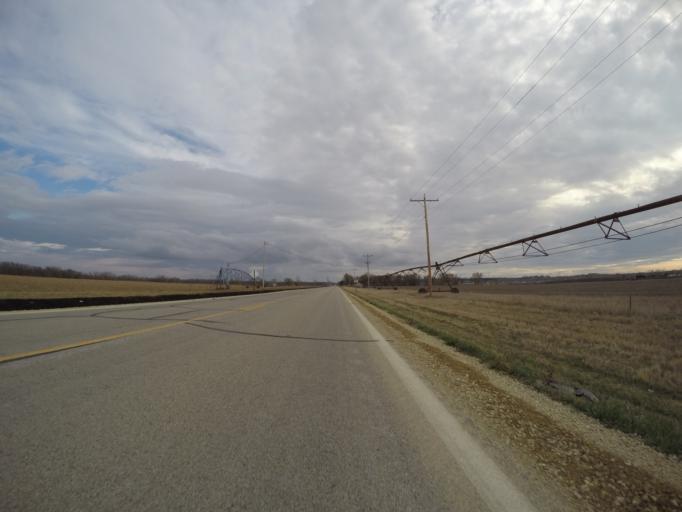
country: US
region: Kansas
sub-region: Riley County
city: Manhattan
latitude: 39.2230
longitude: -96.5578
